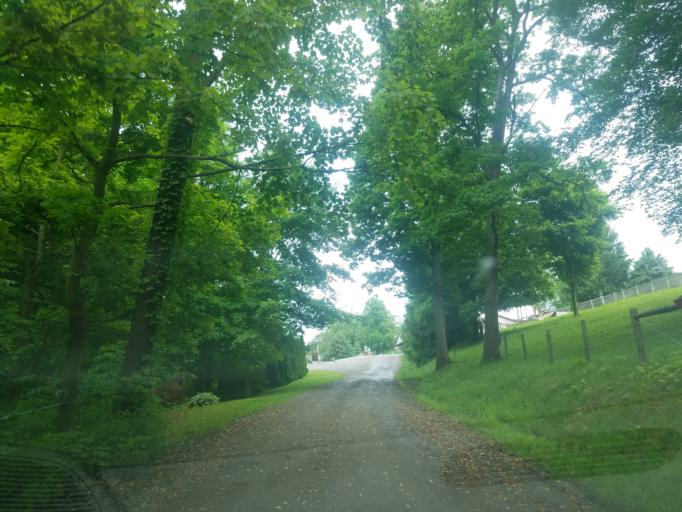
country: US
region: Ohio
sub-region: Holmes County
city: Millersburg
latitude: 40.4797
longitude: -81.8122
